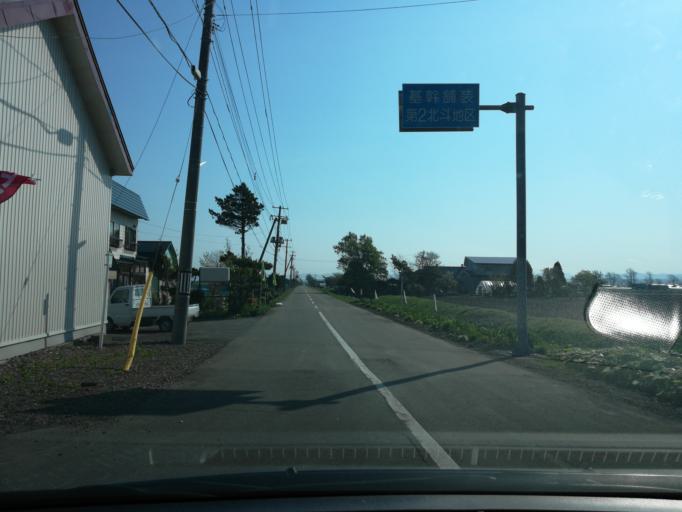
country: JP
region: Hokkaido
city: Iwamizawa
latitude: 43.1340
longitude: 141.6817
